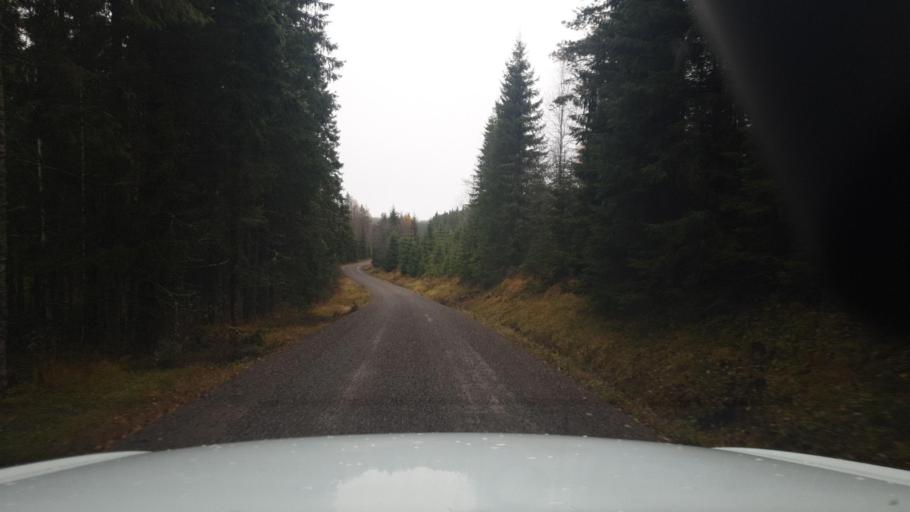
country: SE
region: Vaermland
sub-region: Eda Kommun
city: Charlottenberg
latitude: 60.0539
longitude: 12.6287
